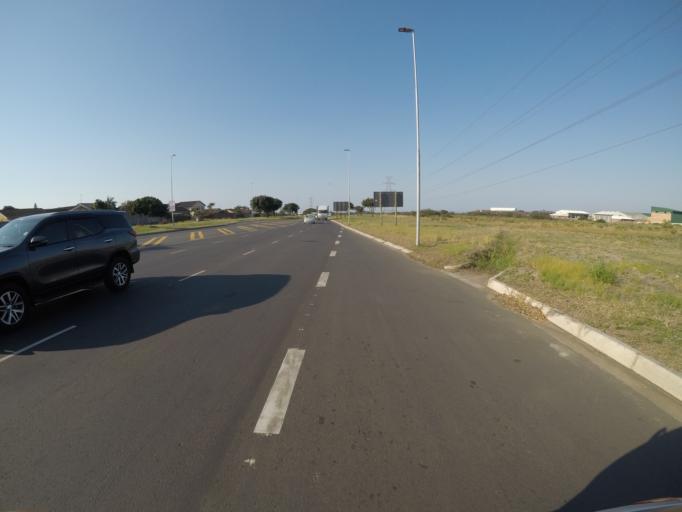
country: ZA
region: KwaZulu-Natal
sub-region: uThungulu District Municipality
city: Richards Bay
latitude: -28.7326
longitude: 32.0391
